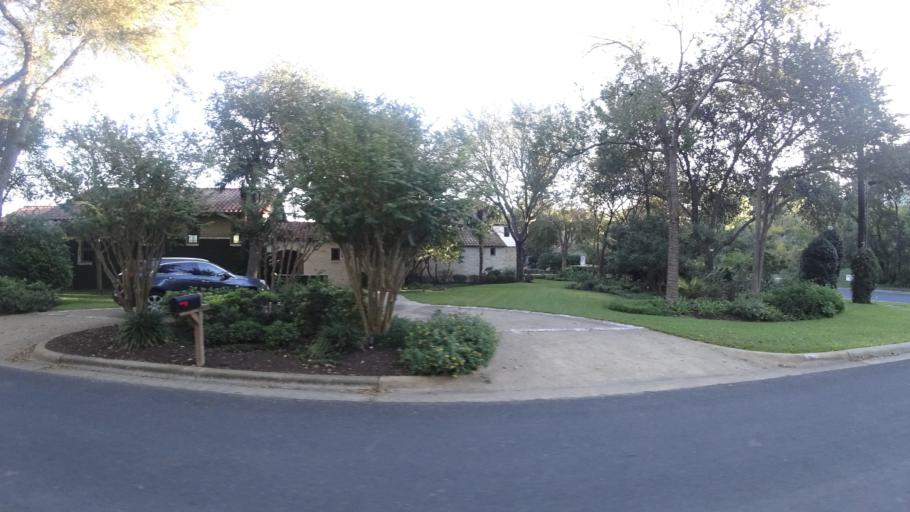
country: US
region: Texas
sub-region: Travis County
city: West Lake Hills
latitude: 30.3056
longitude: -97.7769
